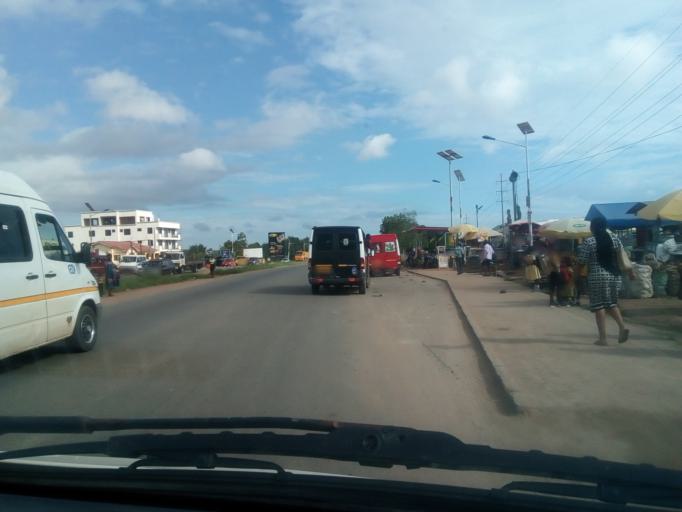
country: GH
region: Greater Accra
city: Achiaman
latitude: 5.6985
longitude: -0.2924
